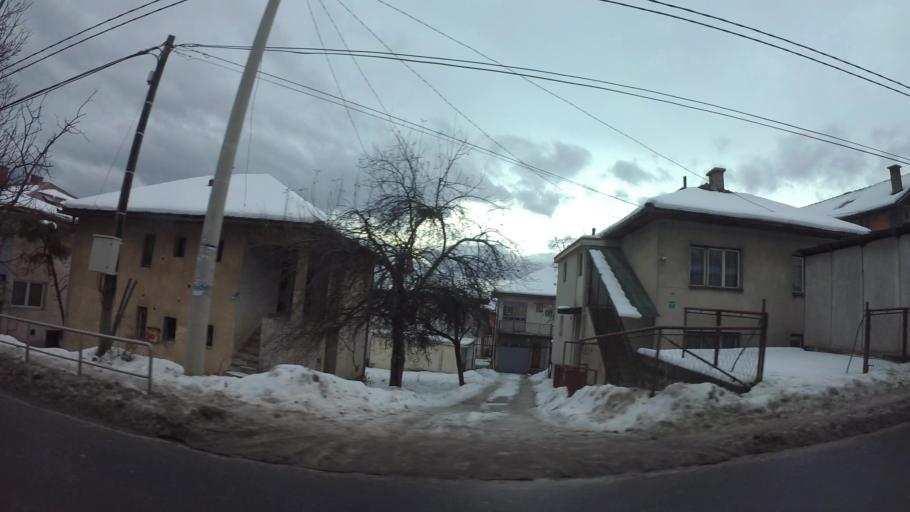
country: BA
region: Federation of Bosnia and Herzegovina
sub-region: Kanton Sarajevo
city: Sarajevo
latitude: 43.8622
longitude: 18.3624
